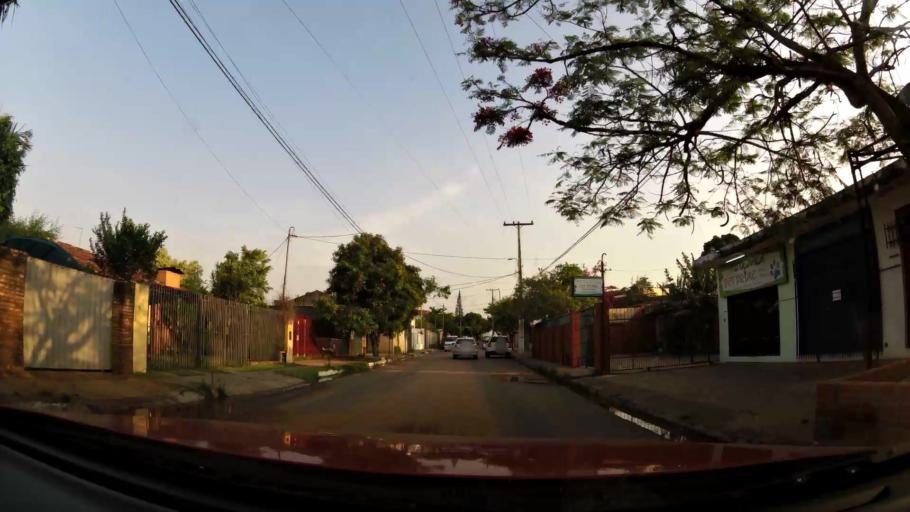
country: PY
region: Central
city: Lambare
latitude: -25.3485
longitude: -57.6062
